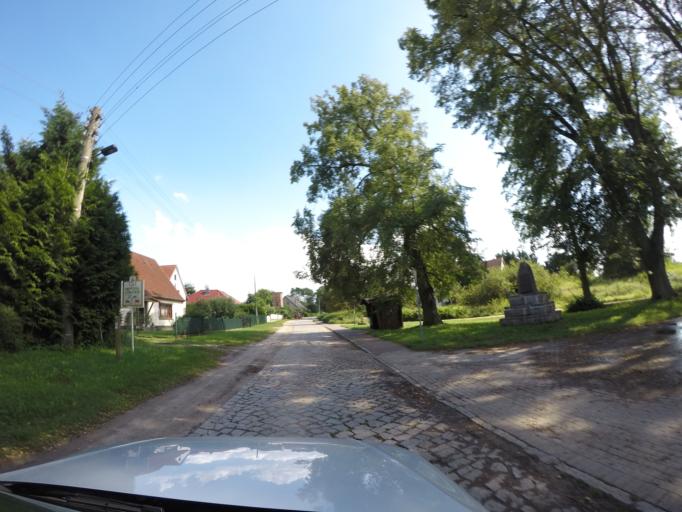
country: DE
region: Mecklenburg-Vorpommern
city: Rechlin
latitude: 53.3426
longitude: 12.8413
